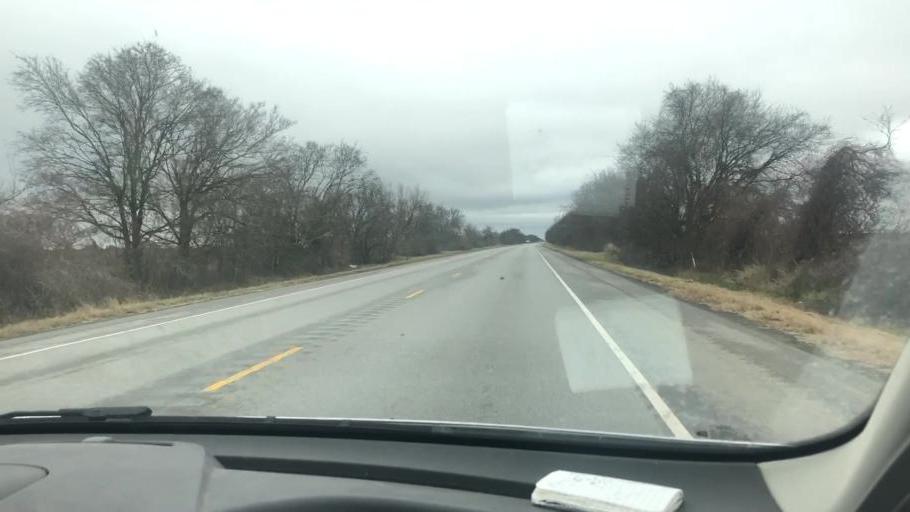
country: US
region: Texas
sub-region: Matagorda County
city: Van Vleck
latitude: 29.1207
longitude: -95.9810
